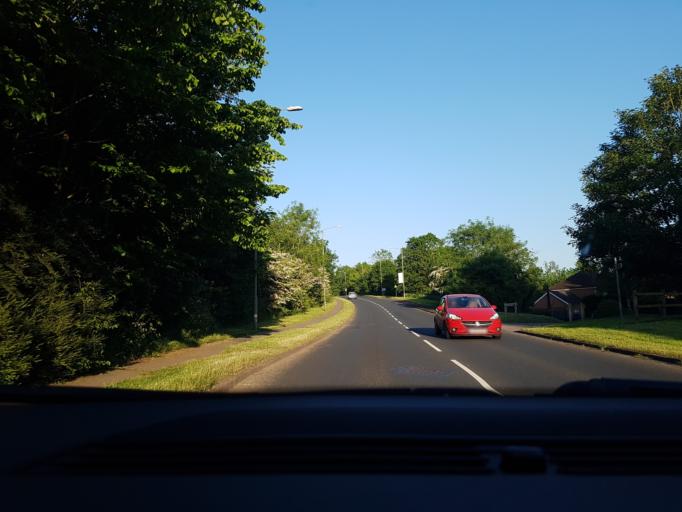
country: GB
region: England
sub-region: Buckinghamshire
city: Buckingham
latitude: 52.0030
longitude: -0.9786
